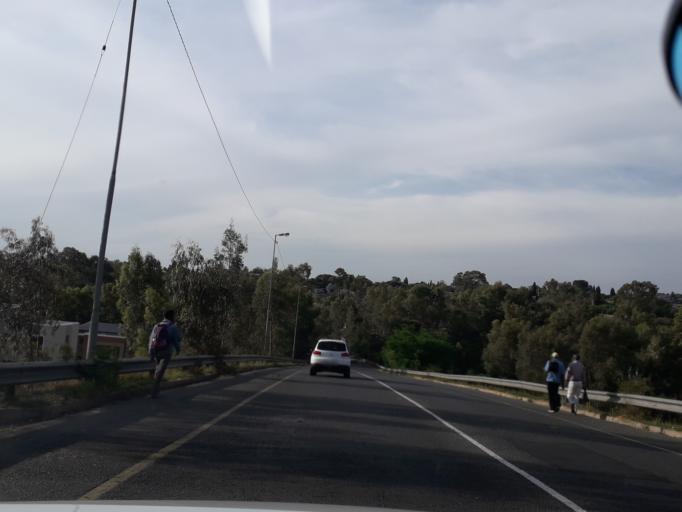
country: ZA
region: Gauteng
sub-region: City of Johannesburg Metropolitan Municipality
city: Diepsloot
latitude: -26.0478
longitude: 27.9991
